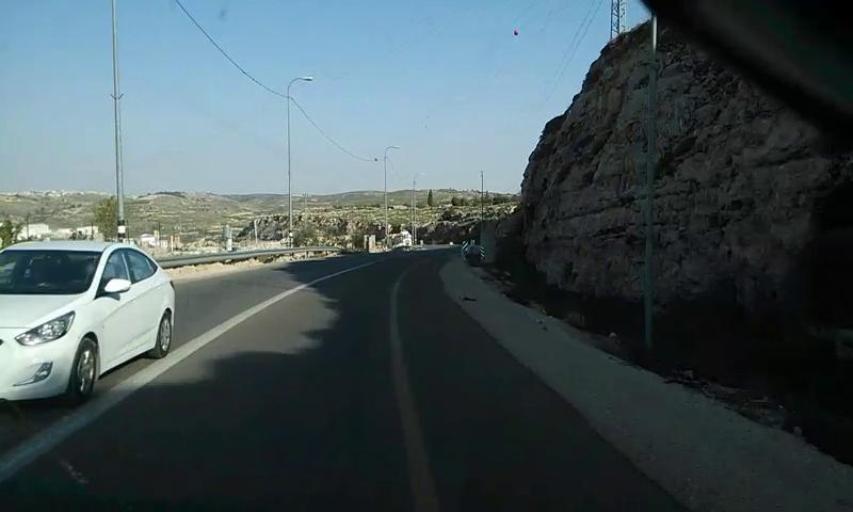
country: PS
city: Khallat ad Dar
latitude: 31.5021
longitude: 35.1111
